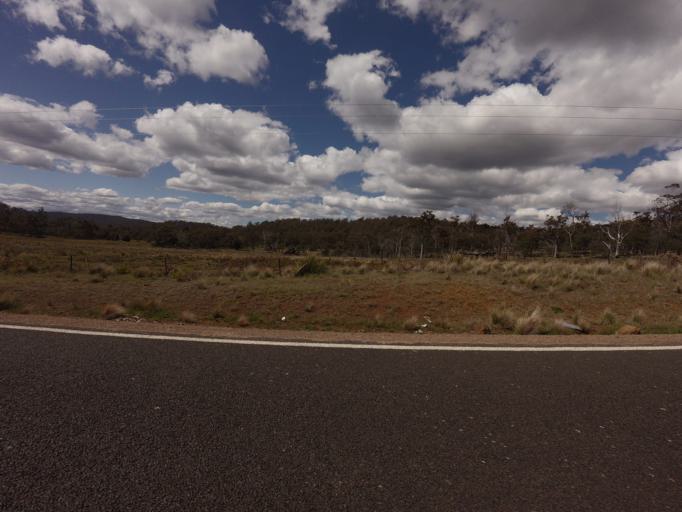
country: AU
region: Tasmania
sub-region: Northern Midlands
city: Evandale
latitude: -41.9554
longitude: 147.6124
